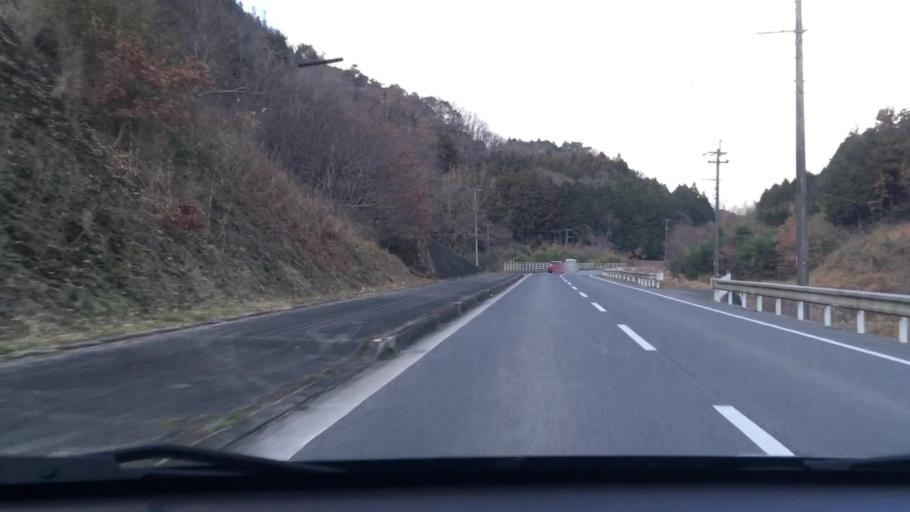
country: JP
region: Oita
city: Bungo-Takada-shi
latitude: 33.4721
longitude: 131.3844
